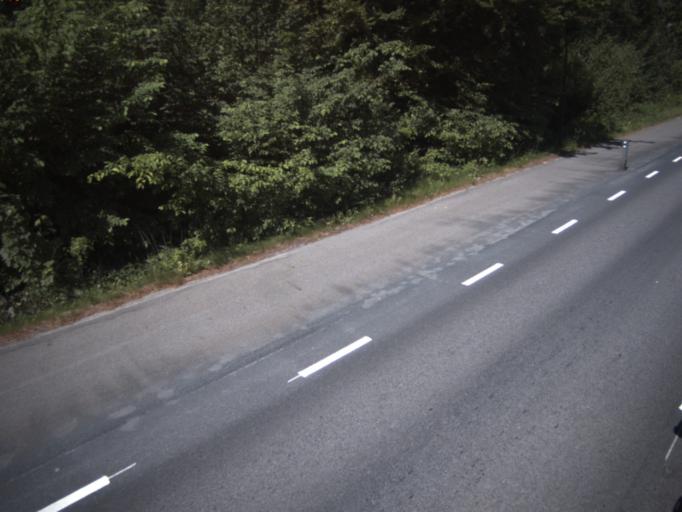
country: DK
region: Capital Region
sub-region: Helsingor Kommune
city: Helsingor
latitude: 56.1094
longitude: 12.6377
